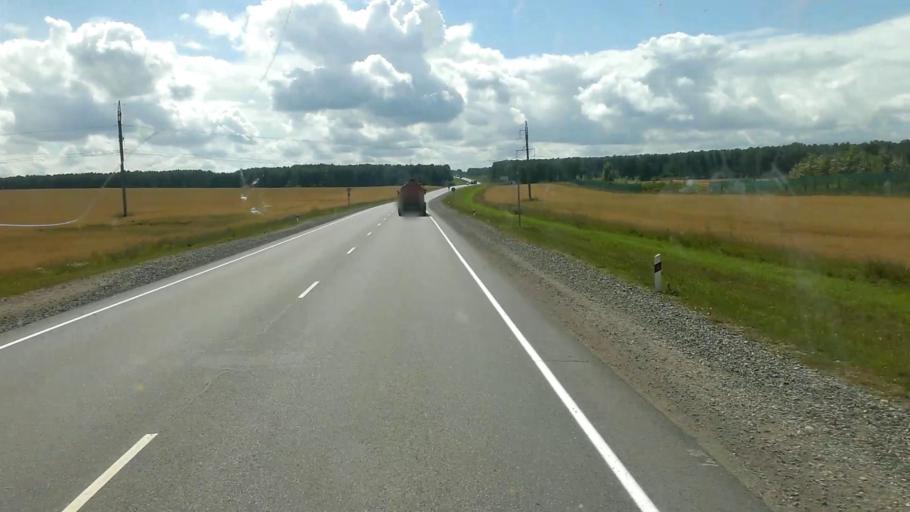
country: RU
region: Altai Krai
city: Troitskoye
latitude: 52.9903
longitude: 84.7425
